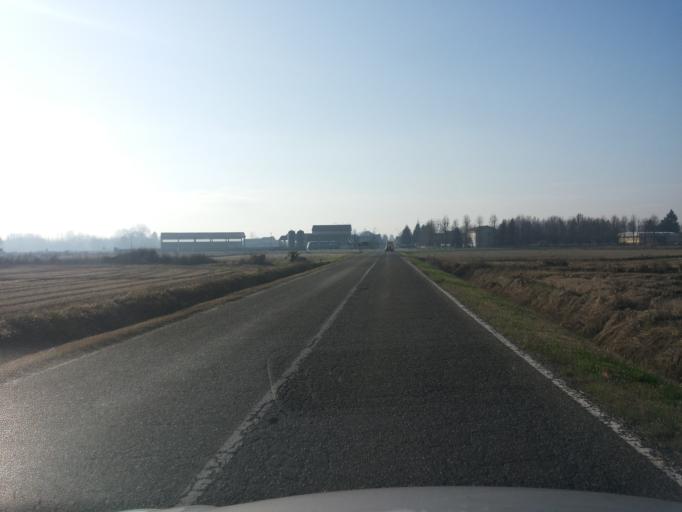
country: IT
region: Piedmont
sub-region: Provincia di Vercelli
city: Desana
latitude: 45.2760
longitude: 8.3650
